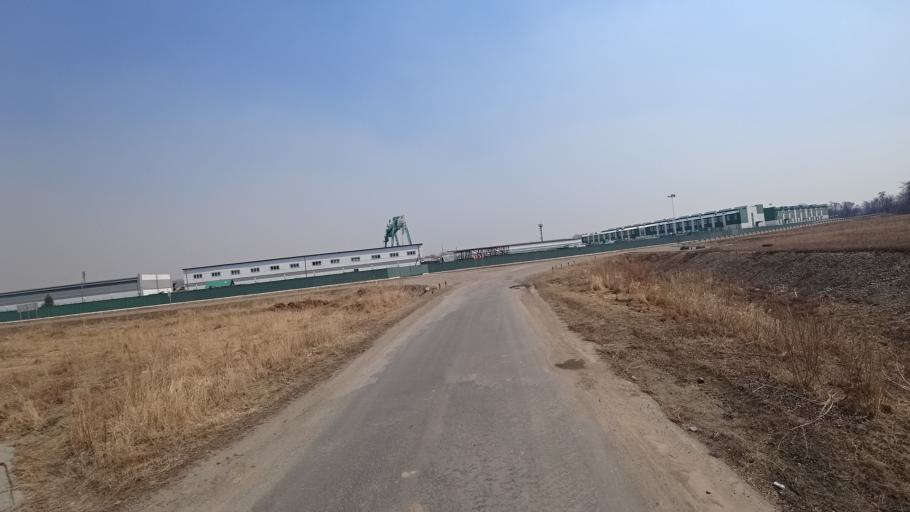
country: RU
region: Amur
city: Novobureyskiy
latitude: 49.7851
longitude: 129.9208
